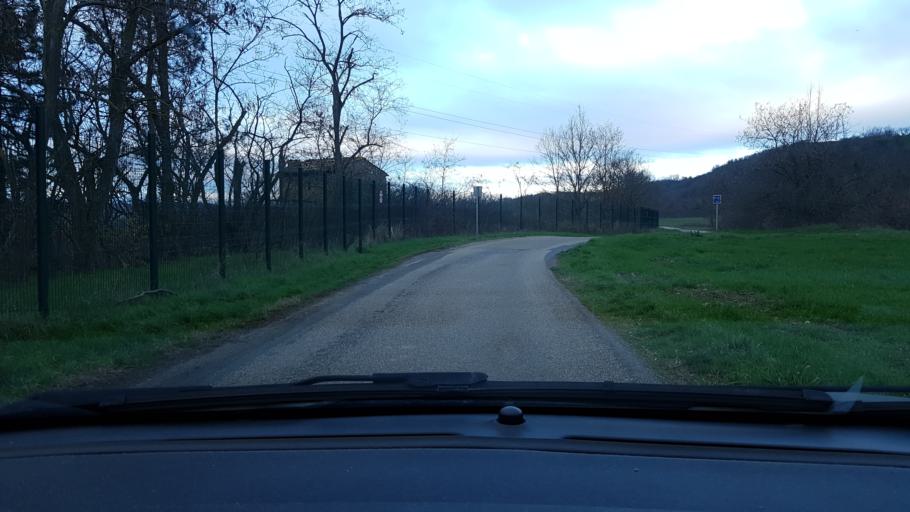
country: FR
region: Rhone-Alpes
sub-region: Departement du Rhone
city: Montagny
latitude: 45.6340
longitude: 4.7690
